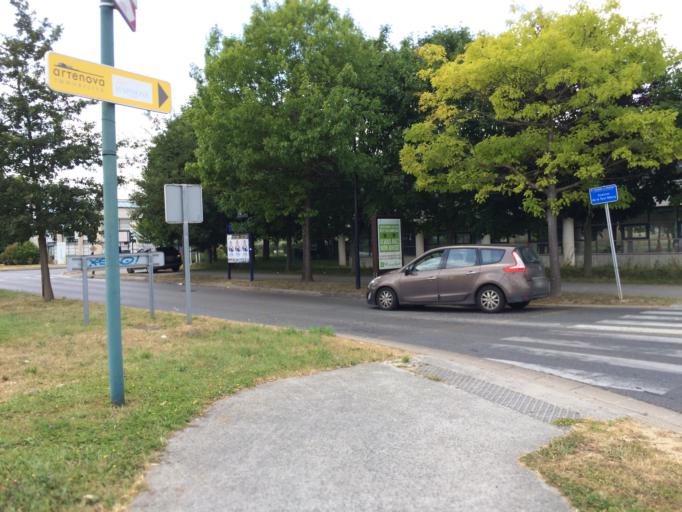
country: FR
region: Ile-de-France
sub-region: Departement de l'Essonne
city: Tigery
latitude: 48.6279
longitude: 2.5169
